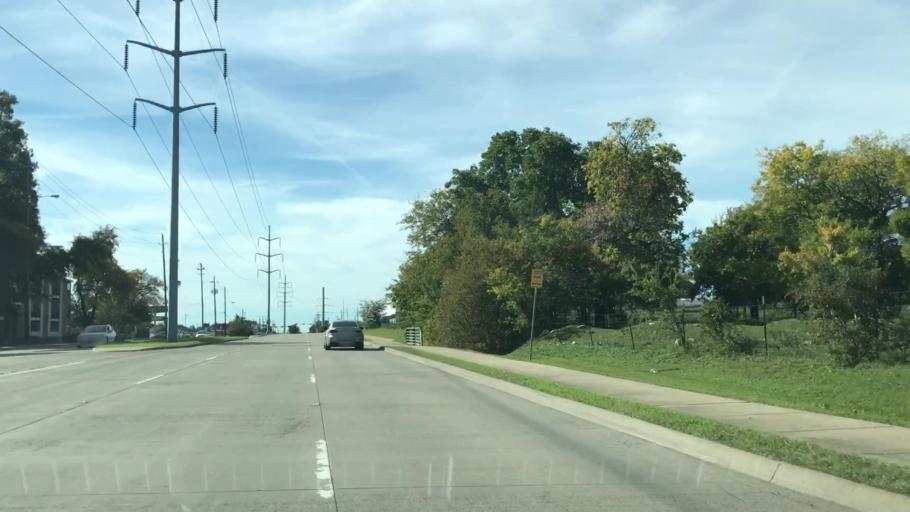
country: US
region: Texas
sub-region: Dallas County
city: Addison
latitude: 33.0118
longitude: -96.8515
